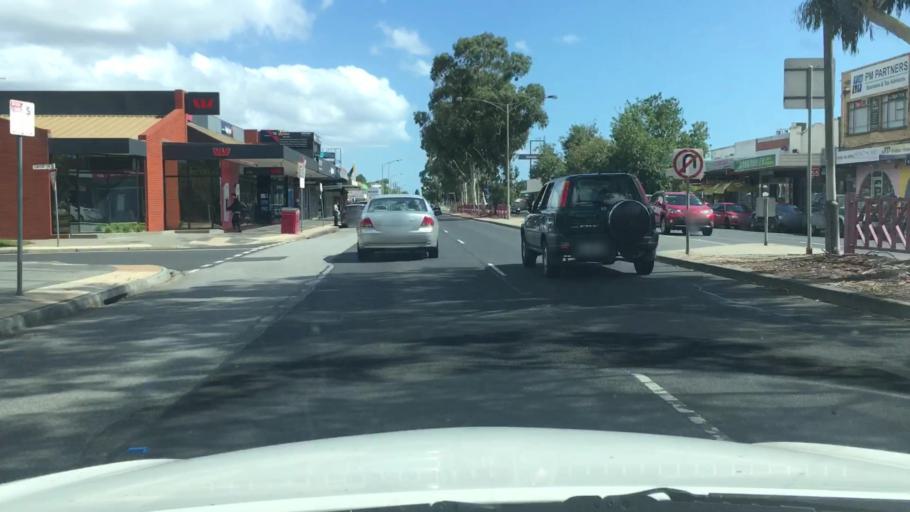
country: AU
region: Victoria
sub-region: Greater Dandenong
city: Springvale
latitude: -37.9522
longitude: 145.1524
